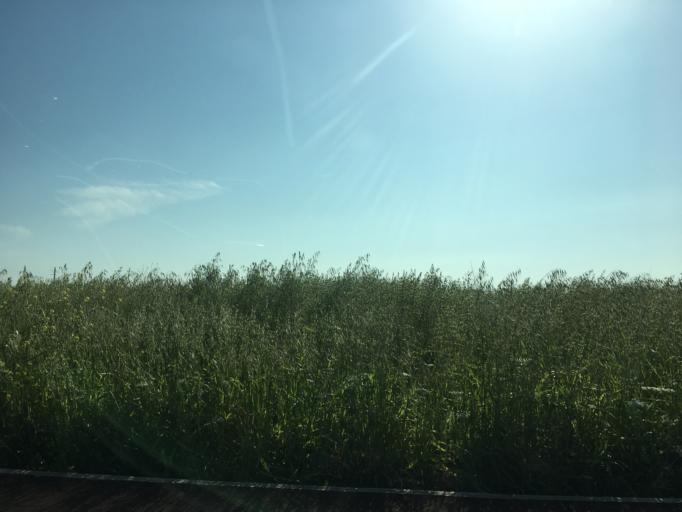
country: PT
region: Lisbon
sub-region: Cascais
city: Parede
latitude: 38.7325
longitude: -9.3565
